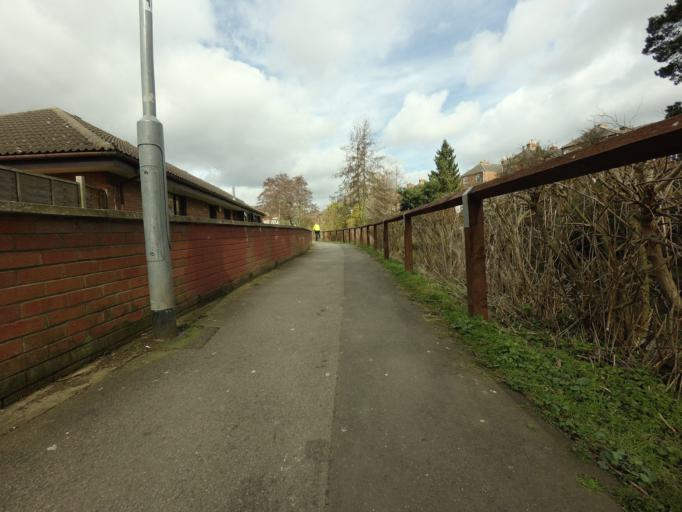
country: GB
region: England
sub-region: Lincolnshire
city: Grantham
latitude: 52.9075
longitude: -0.6347
